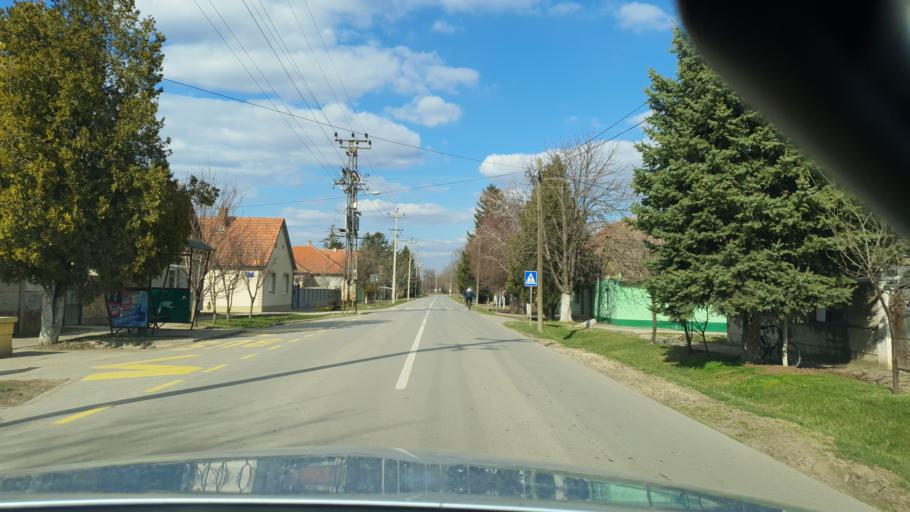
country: RS
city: Kulpin
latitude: 45.4061
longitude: 19.5899
